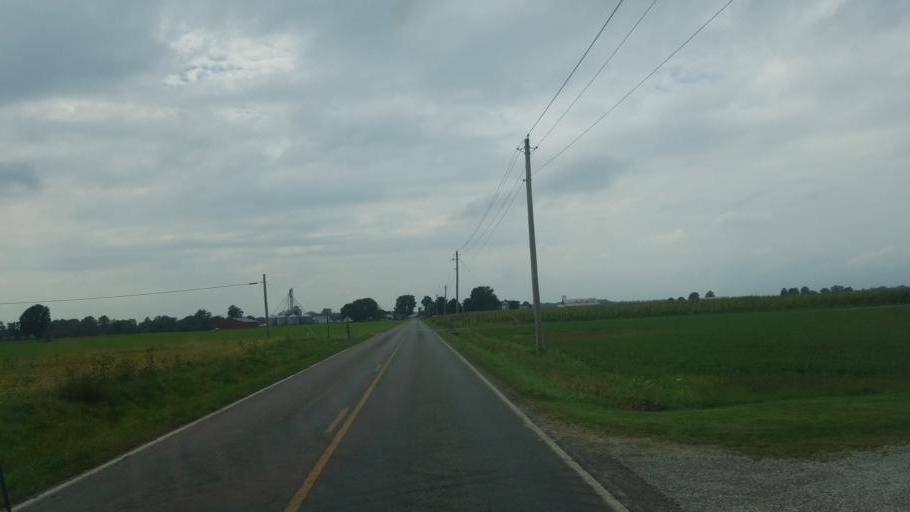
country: US
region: Ohio
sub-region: Medina County
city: Seville
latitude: 40.9604
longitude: -81.8496
